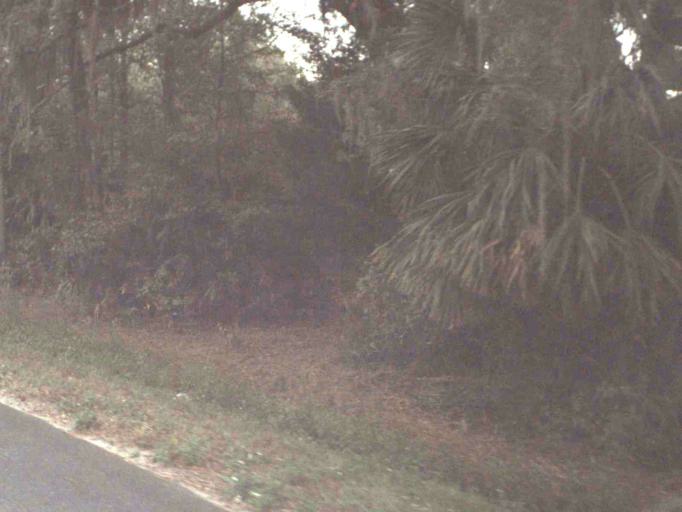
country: US
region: Florida
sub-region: Wakulla County
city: Crawfordville
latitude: 30.0905
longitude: -84.3857
